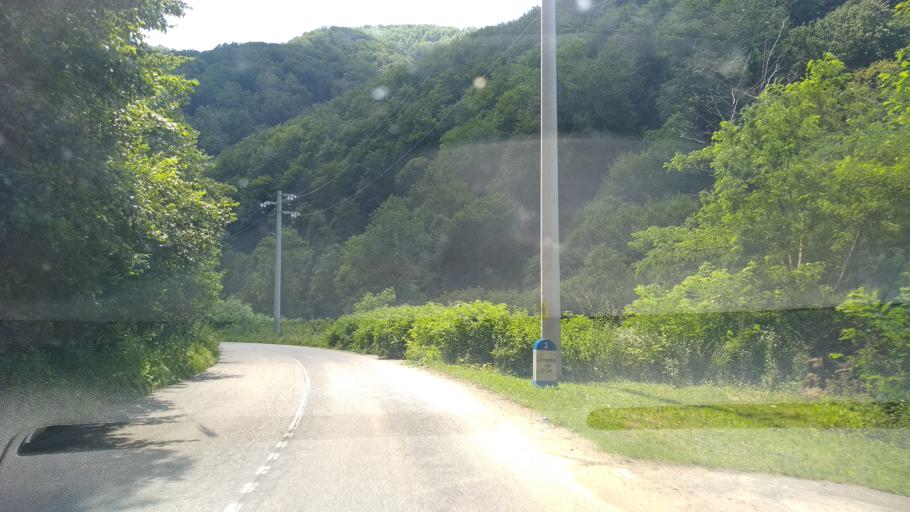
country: RO
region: Hunedoara
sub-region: Comuna Orastioara de Sus
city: Orastioara de Sus
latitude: 45.6687
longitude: 23.1714
